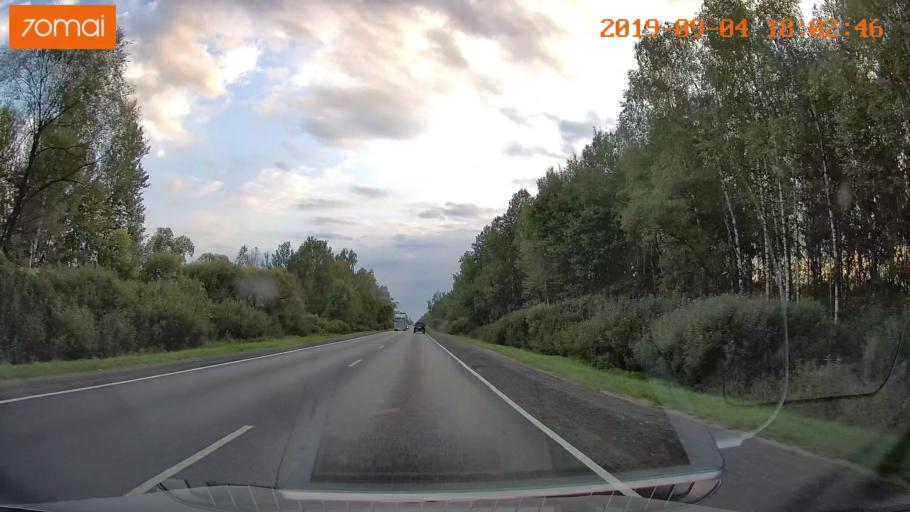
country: RU
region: Moskovskaya
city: Il'inskiy Pogost
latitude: 55.4706
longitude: 38.8606
